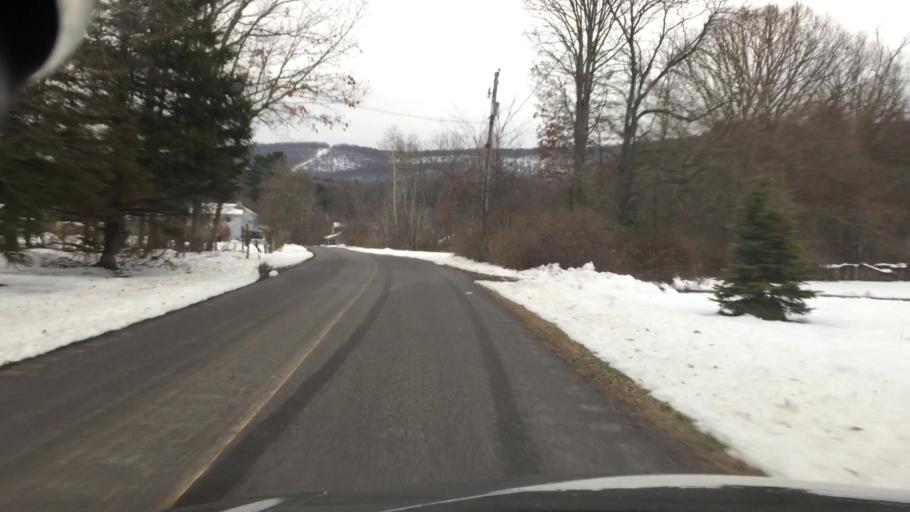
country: US
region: Pennsylvania
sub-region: Luzerne County
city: Conyngham
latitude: 41.0076
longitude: -76.1218
